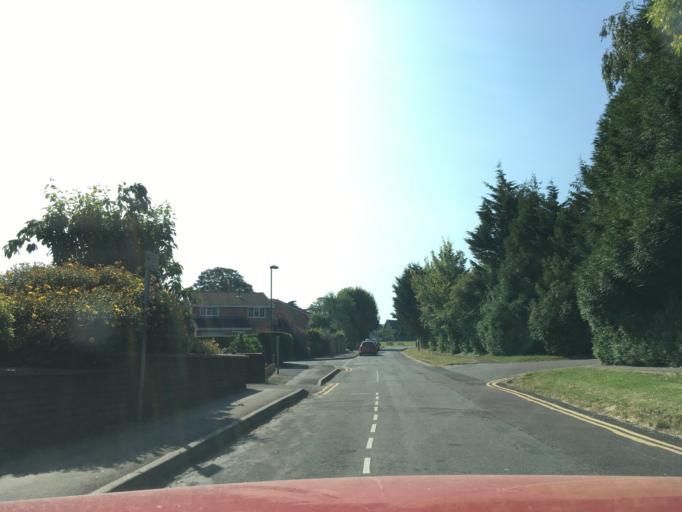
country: GB
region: England
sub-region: South Gloucestershire
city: Stoke Gifford
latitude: 51.5169
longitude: -2.5464
